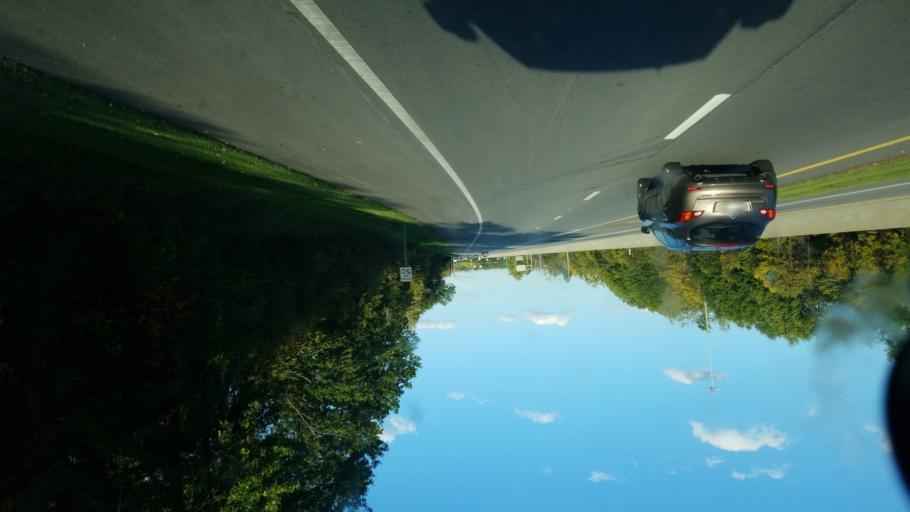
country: US
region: Ohio
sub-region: Franklin County
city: Gahanna
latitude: 40.0178
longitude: -82.8975
